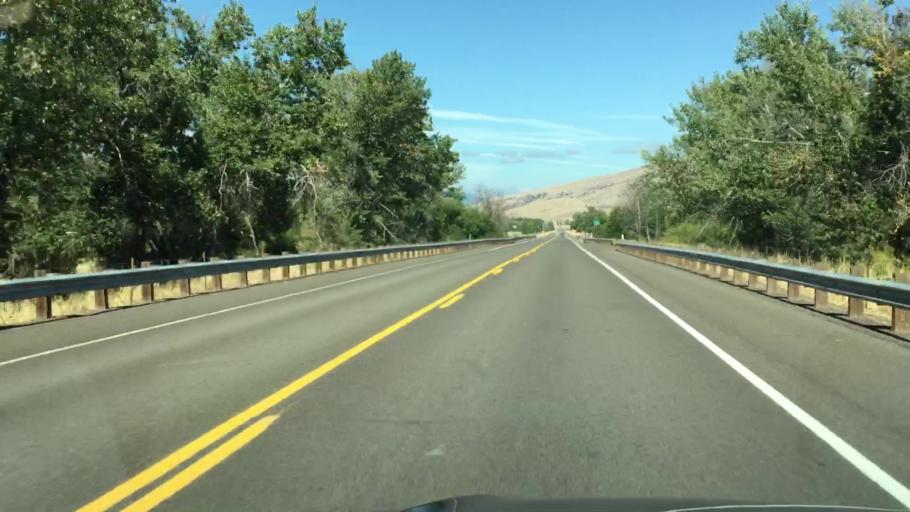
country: US
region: Oregon
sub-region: Wasco County
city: The Dalles
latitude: 45.2404
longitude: -121.1505
